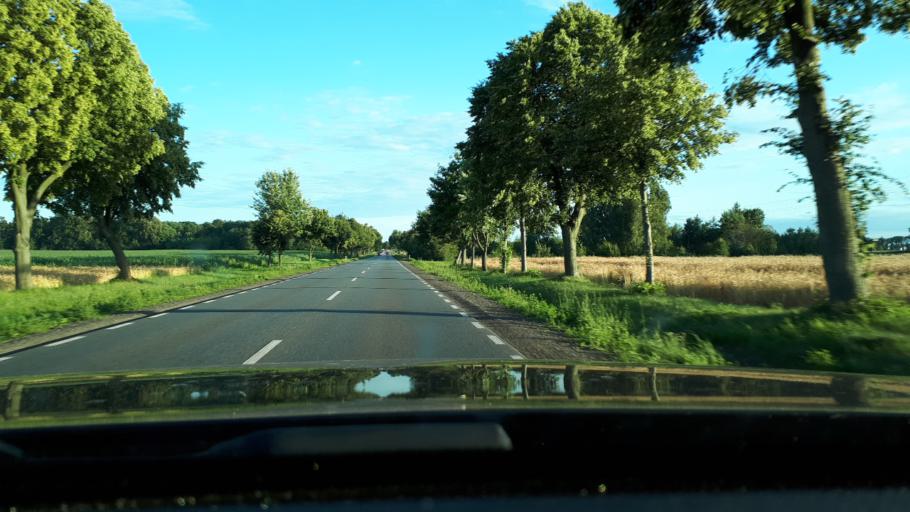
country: PL
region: Masovian Voivodeship
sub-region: Powiat ciechanowski
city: Ciechanow
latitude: 52.8374
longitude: 20.6198
